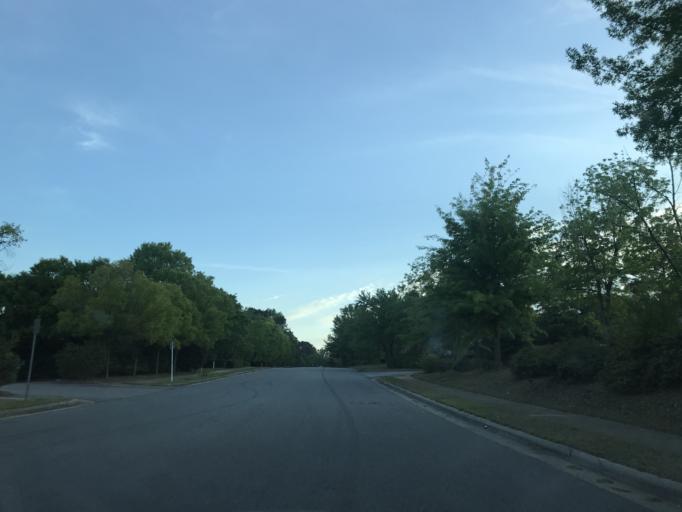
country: US
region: North Carolina
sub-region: Wake County
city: Knightdale
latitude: 35.7661
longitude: -78.5525
